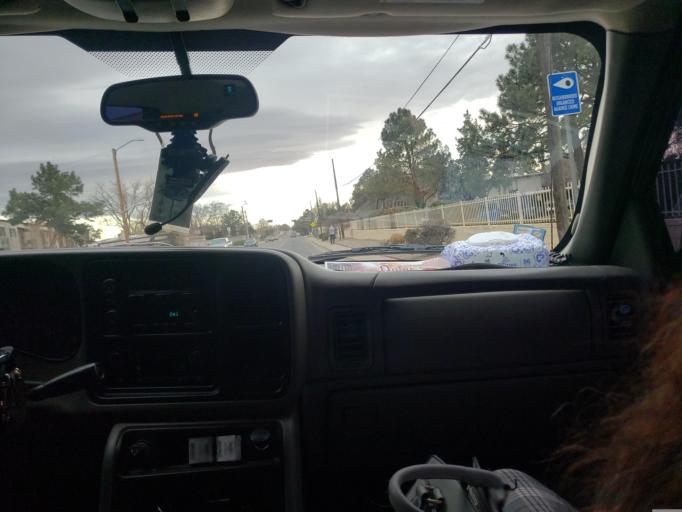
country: US
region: New Mexico
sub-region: Bernalillo County
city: Albuquerque
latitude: 35.0994
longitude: -106.5598
